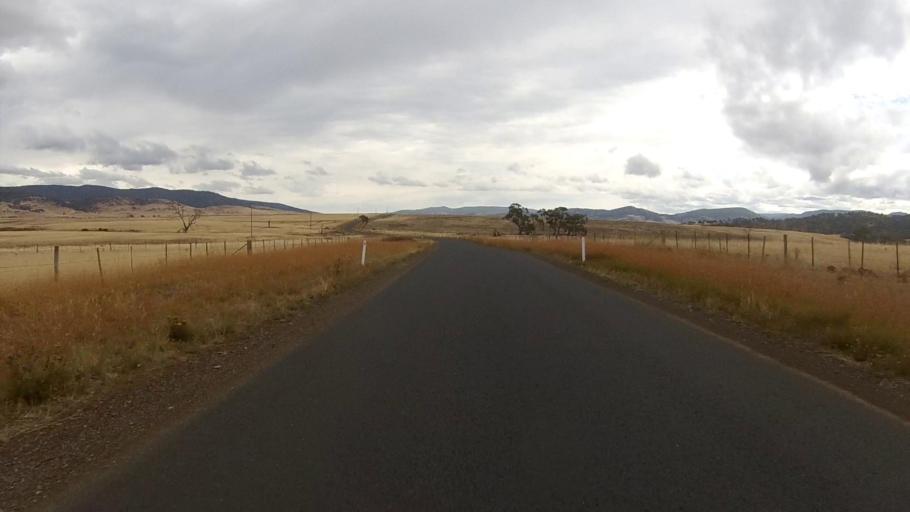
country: AU
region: Tasmania
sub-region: Northern Midlands
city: Evandale
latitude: -41.8264
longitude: 147.7802
